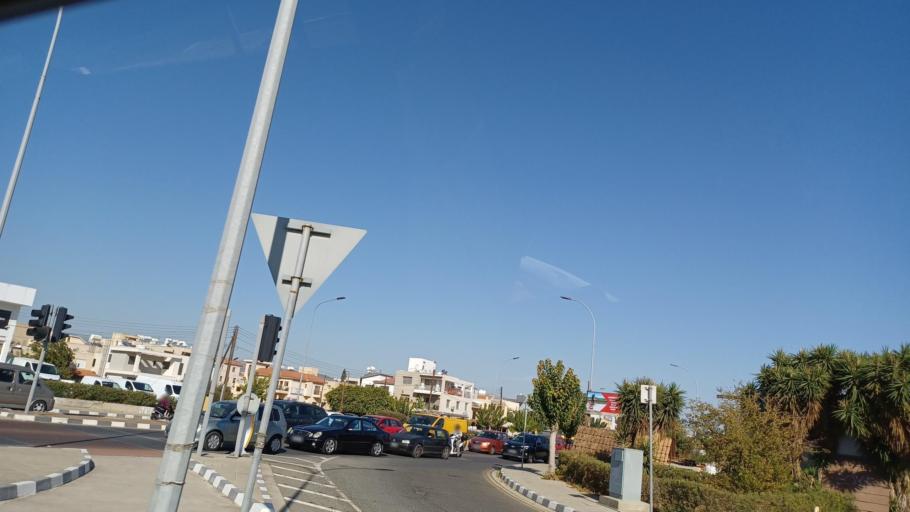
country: CY
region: Limassol
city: Pano Polemidia
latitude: 34.6770
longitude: 32.9995
